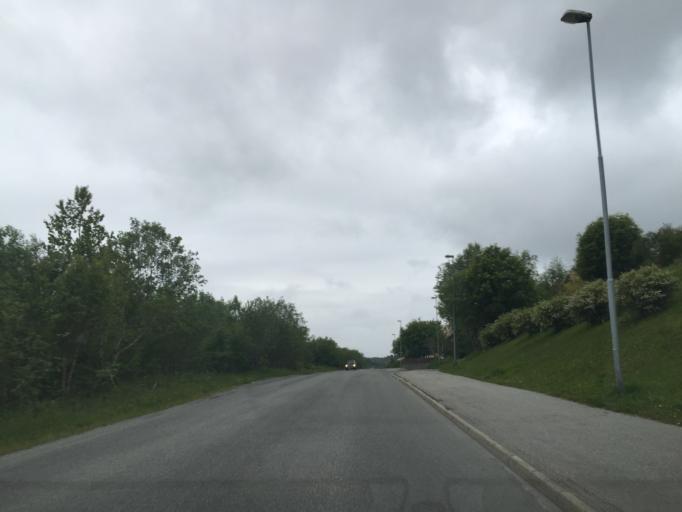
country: NO
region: Nordland
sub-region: Bodo
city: Loding
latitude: 67.2951
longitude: 14.5962
